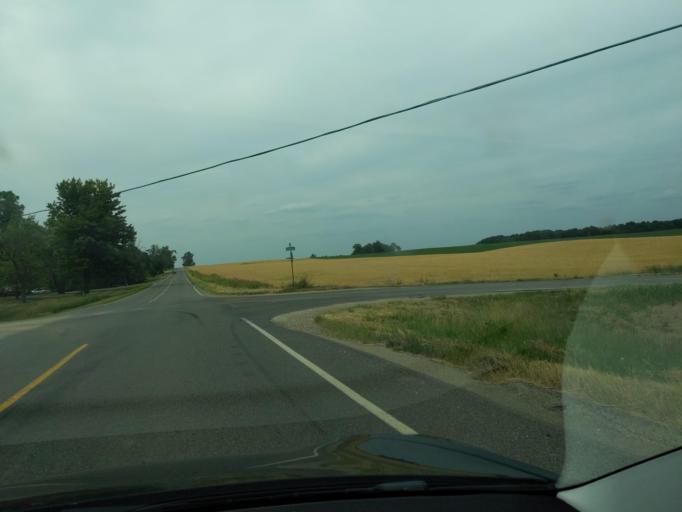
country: US
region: Michigan
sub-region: Clinton County
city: DeWitt
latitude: 42.8563
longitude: -84.6025
